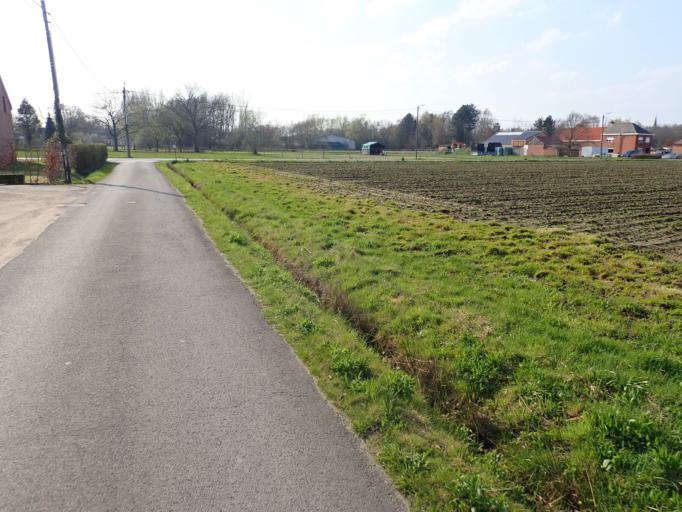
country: BE
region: Flanders
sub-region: Provincie Antwerpen
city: Heist-op-den-Berg
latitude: 51.0415
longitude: 4.7304
